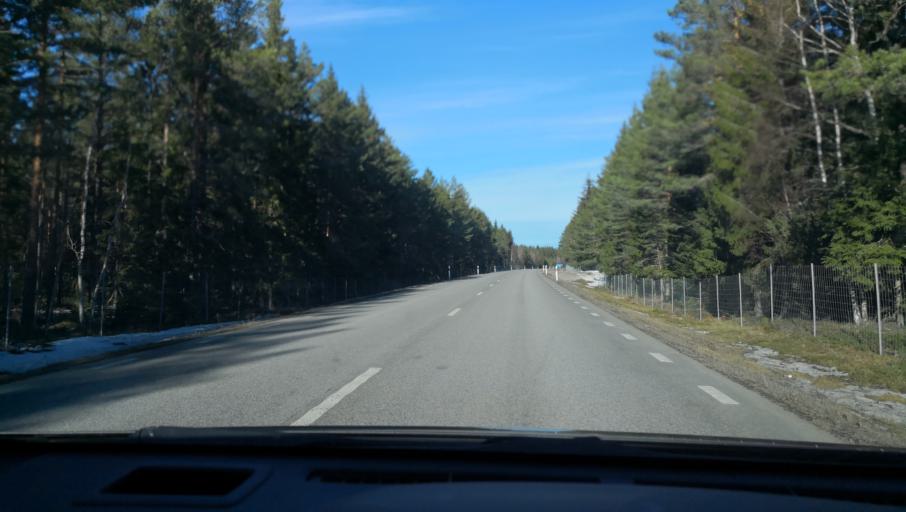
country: SE
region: Uppsala
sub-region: Uppsala Kommun
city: Vattholma
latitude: 60.0482
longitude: 17.7512
